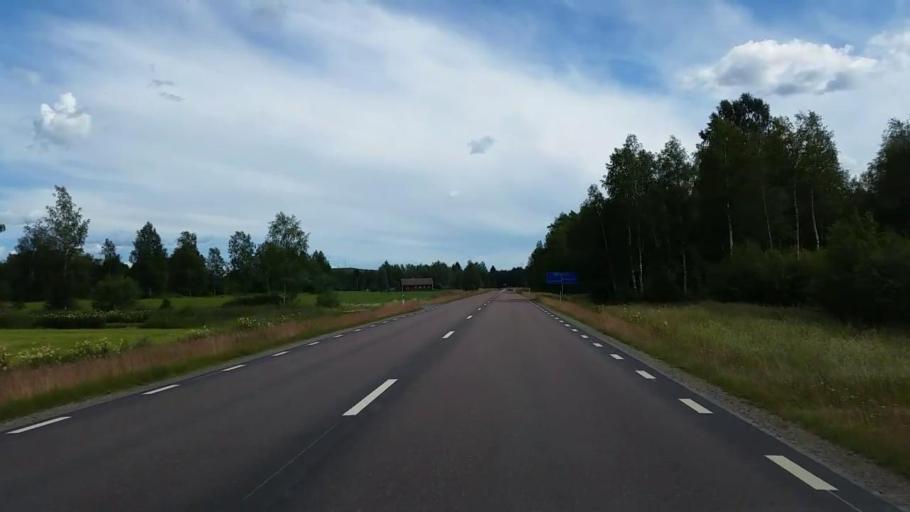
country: SE
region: Gaevleborg
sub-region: Ovanakers Kommun
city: Edsbyn
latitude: 61.3648
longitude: 15.8849
